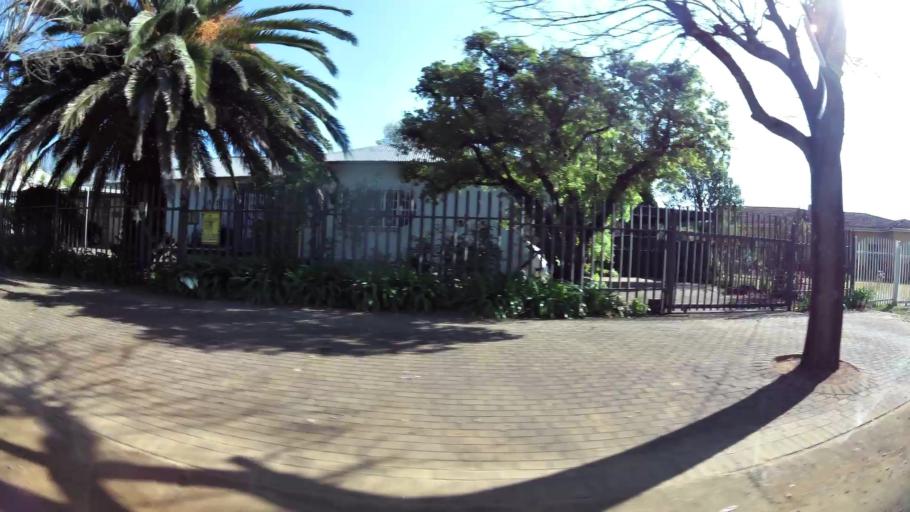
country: ZA
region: Gauteng
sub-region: Ekurhuleni Metropolitan Municipality
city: Benoni
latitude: -26.1544
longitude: 28.3300
